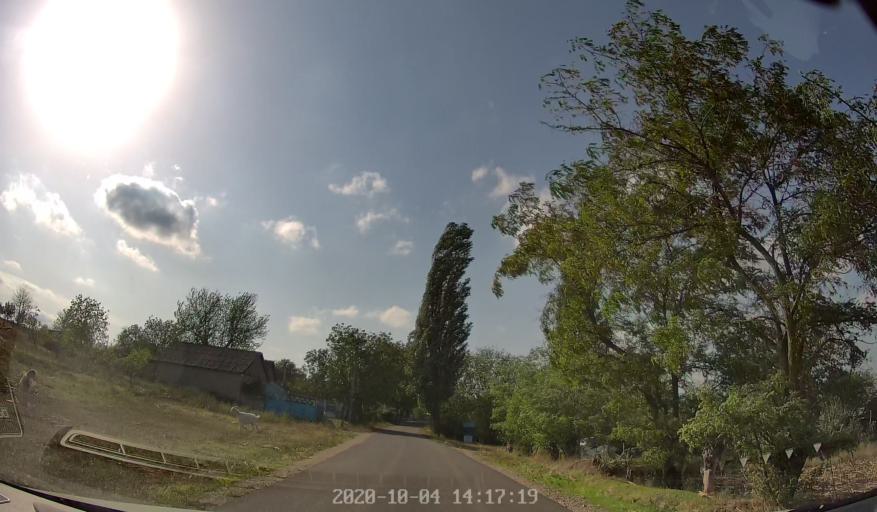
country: MD
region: Rezina
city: Saharna
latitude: 47.6016
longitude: 28.9826
